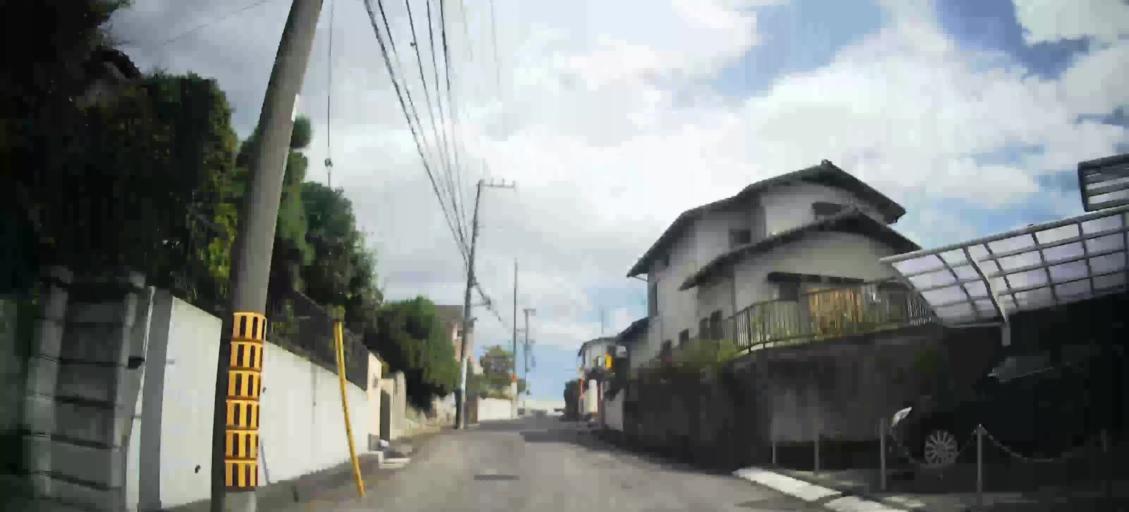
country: JP
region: Kanagawa
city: Minami-rinkan
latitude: 35.4882
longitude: 139.5474
